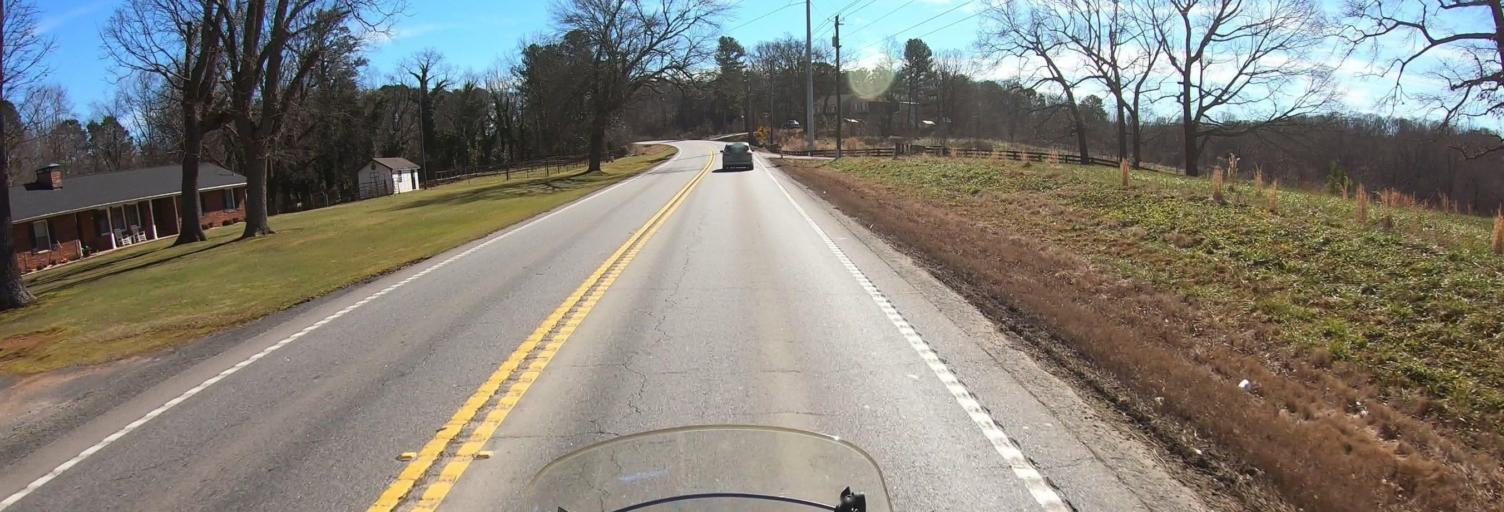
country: US
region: Georgia
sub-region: Forsyth County
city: Cumming
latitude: 34.2853
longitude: -84.1349
